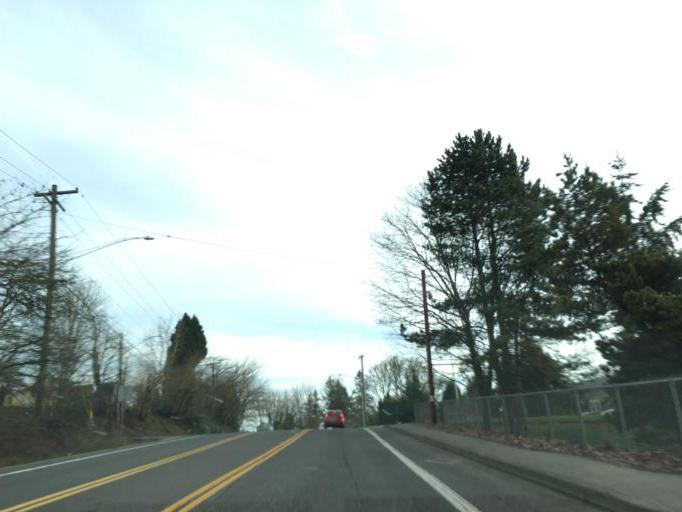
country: US
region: Oregon
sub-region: Clackamas County
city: Lake Oswego
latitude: 45.4554
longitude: -122.6844
